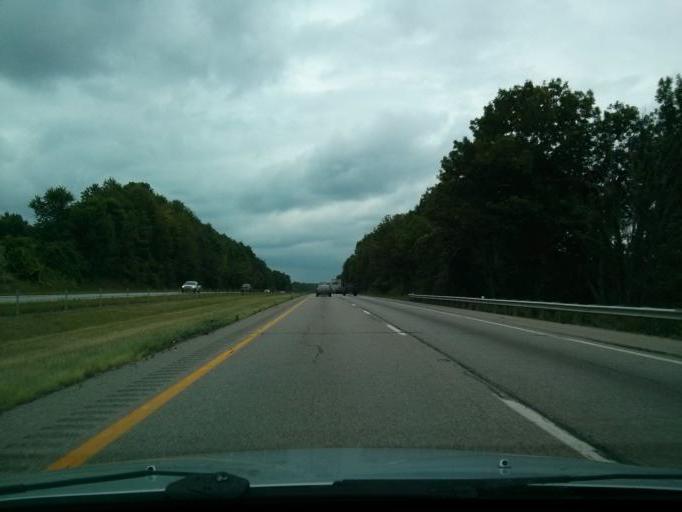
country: US
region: Ohio
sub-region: Portage County
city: Ravenna
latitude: 41.1058
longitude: -81.2038
